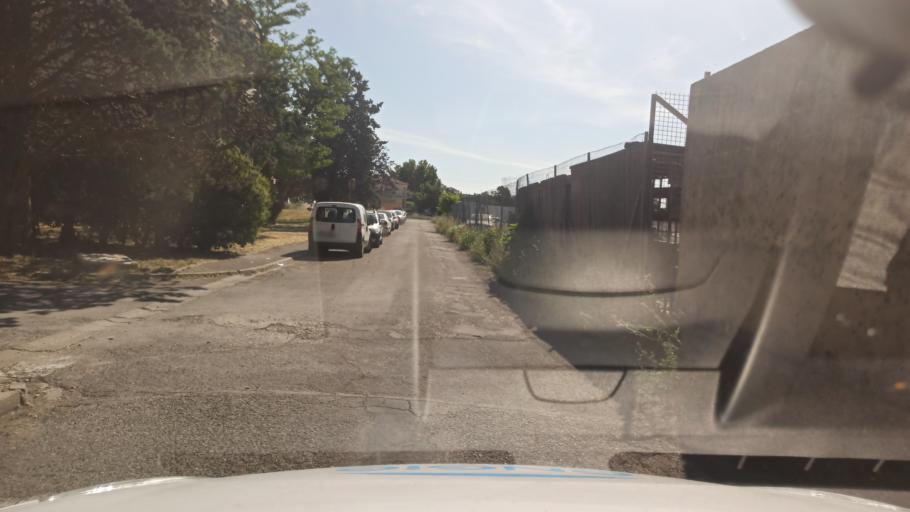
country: FR
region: Provence-Alpes-Cote d'Azur
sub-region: Departement du Vaucluse
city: Le Pontet
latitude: 43.9585
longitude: 4.8492
